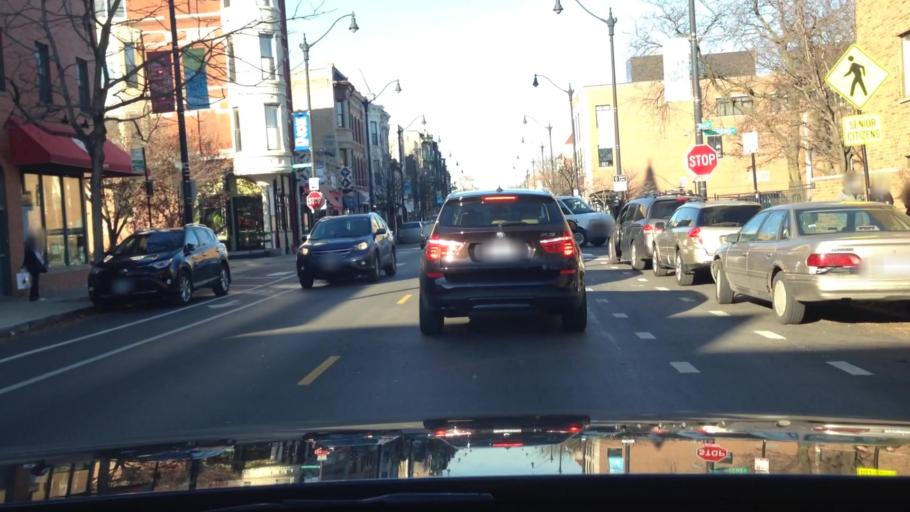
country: US
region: Illinois
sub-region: Cook County
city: Chicago
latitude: 41.9196
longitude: -87.6486
